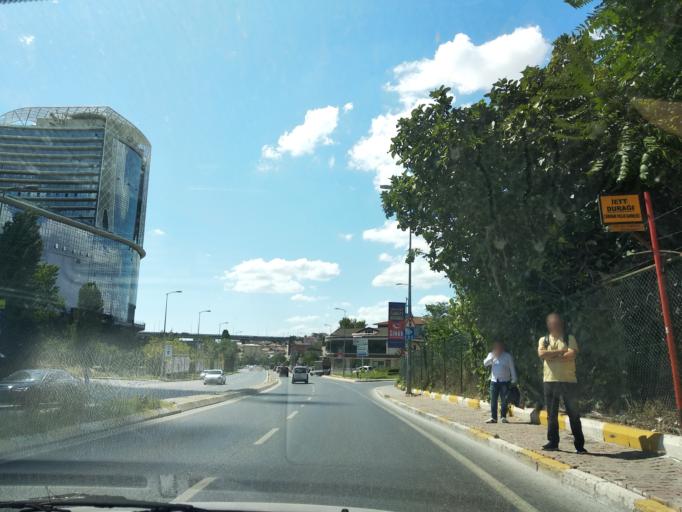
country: TR
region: Istanbul
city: Umraniye
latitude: 41.0070
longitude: 29.1085
